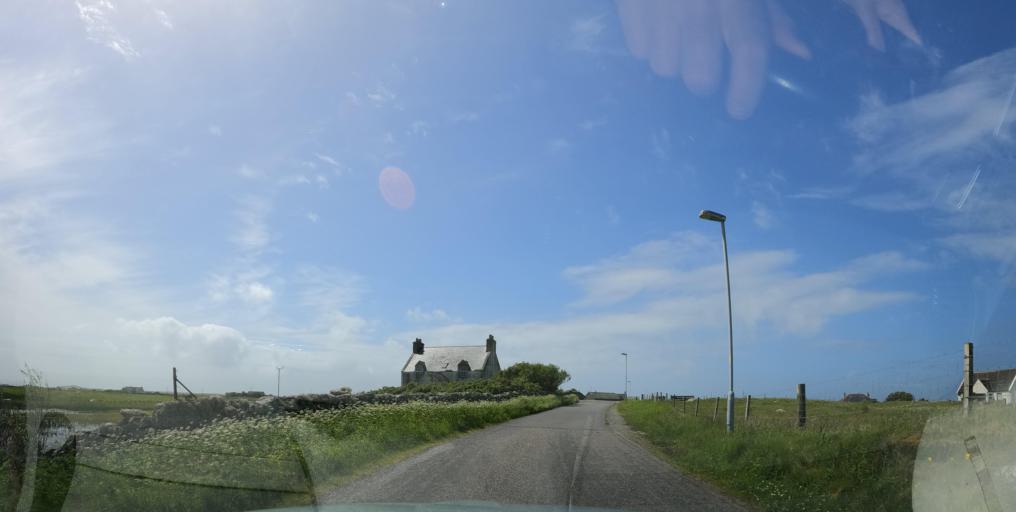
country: GB
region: Scotland
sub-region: Eilean Siar
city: Isle of South Uist
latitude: 57.1654
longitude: -7.3797
